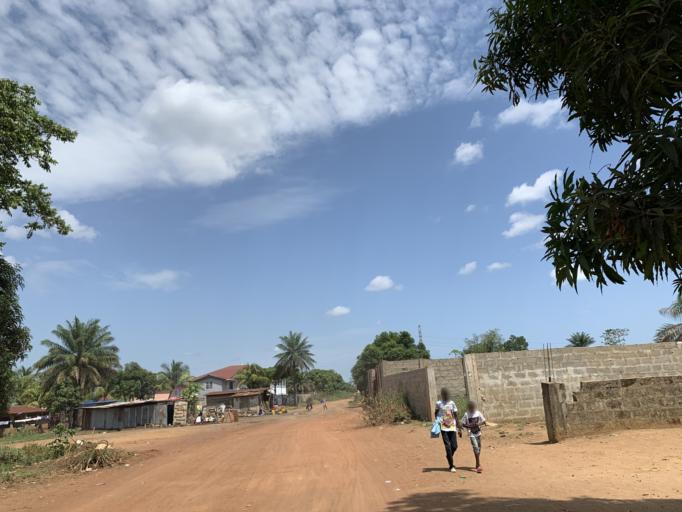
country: SL
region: Western Area
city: Waterloo
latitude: 8.3297
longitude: -13.0400
